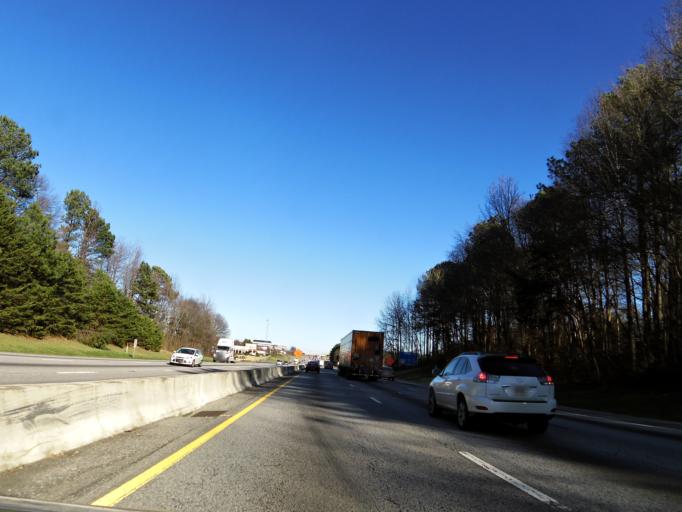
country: US
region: South Carolina
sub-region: Greenville County
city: Five Forks
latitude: 34.8545
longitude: -82.2715
